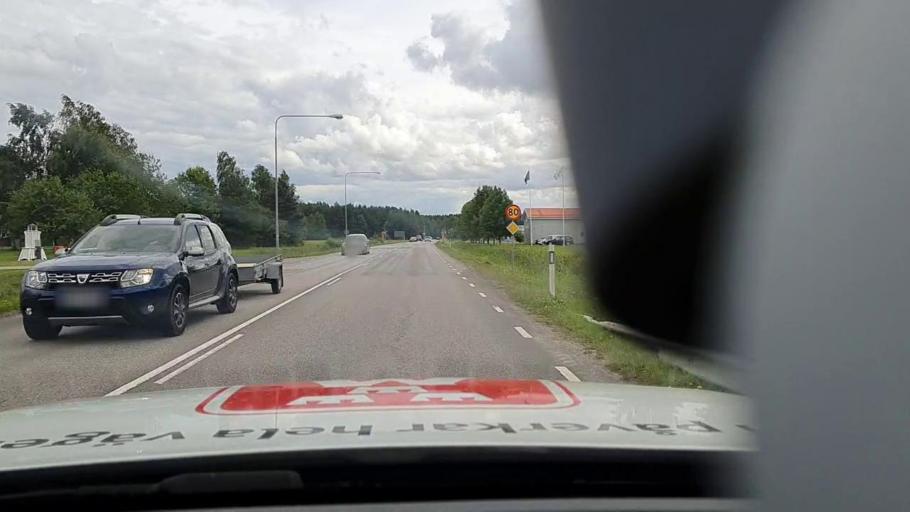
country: SE
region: Vaestra Goetaland
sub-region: Lidkopings Kommun
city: Lidkoping
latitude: 58.5023
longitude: 13.1263
